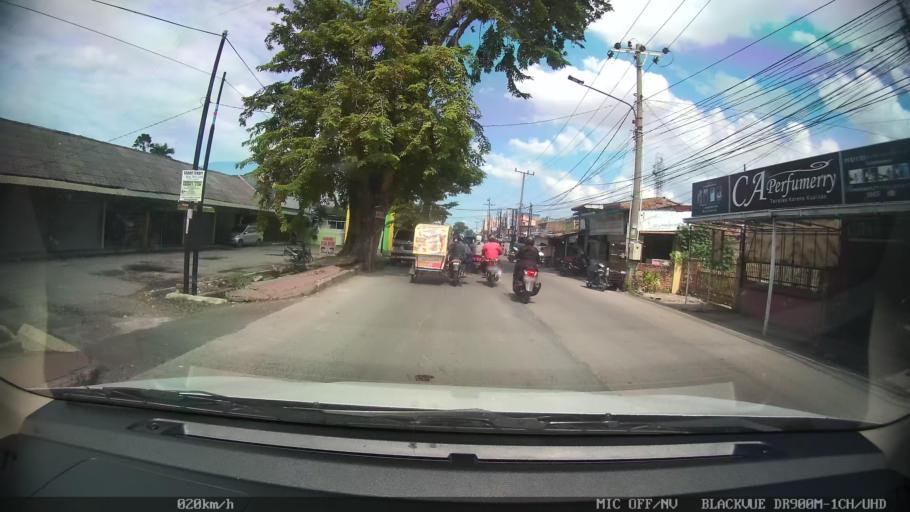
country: ID
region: North Sumatra
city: Medan
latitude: 3.6047
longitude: 98.6441
